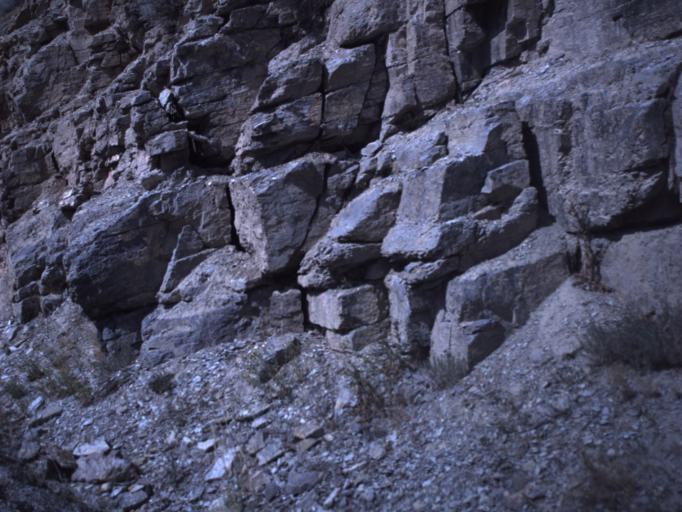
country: US
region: Utah
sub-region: Cache County
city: North Logan
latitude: 41.8277
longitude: -111.6019
